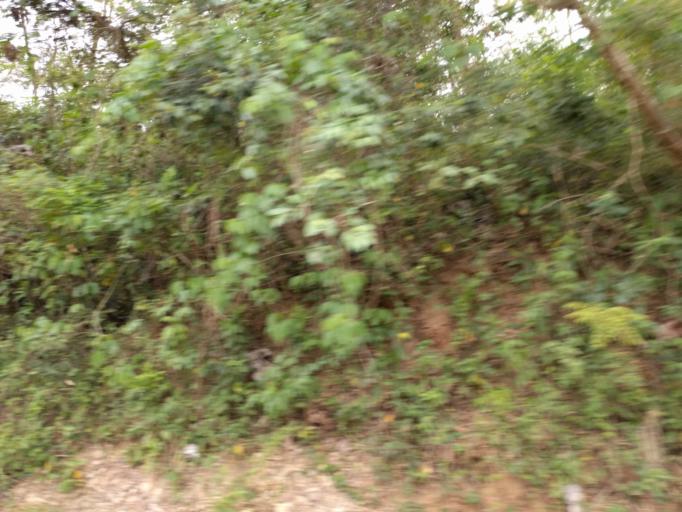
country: BO
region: Santa Cruz
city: Santiago del Torno
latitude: -17.9299
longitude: -63.4140
